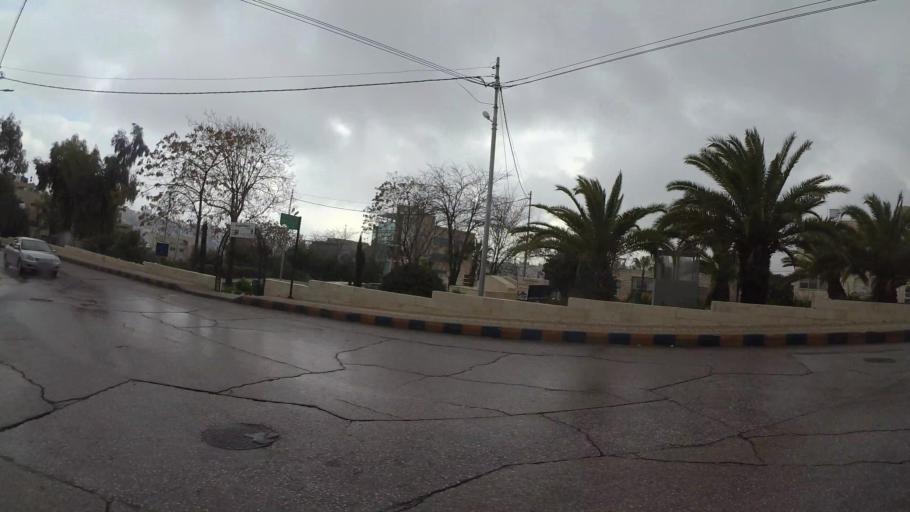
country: JO
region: Amman
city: Amman
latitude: 31.9486
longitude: 35.9072
